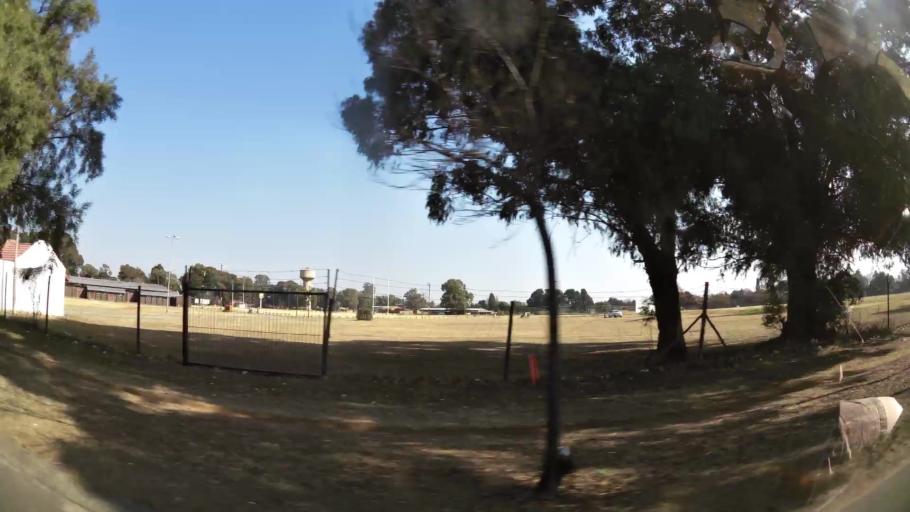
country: ZA
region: Gauteng
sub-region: West Rand District Municipality
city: Randfontein
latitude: -26.1615
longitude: 27.7050
